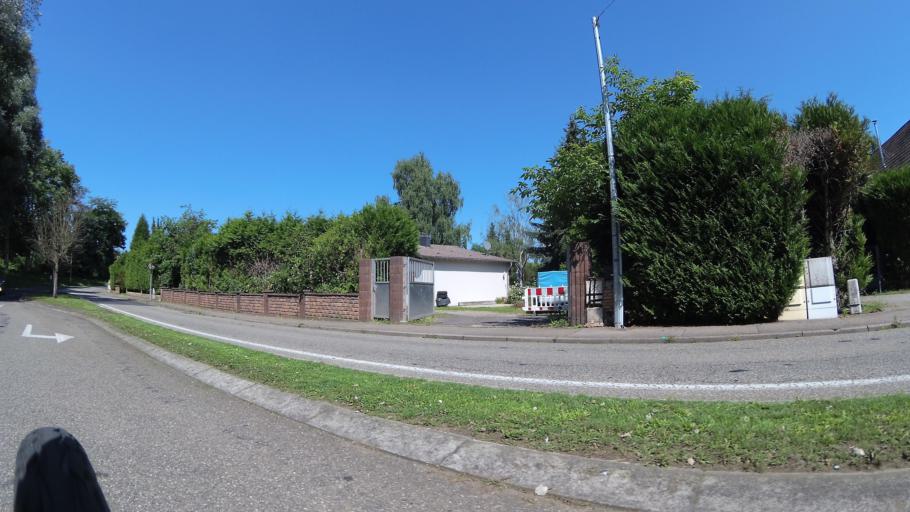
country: FR
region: Lorraine
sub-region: Departement de la Moselle
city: Stiring-Wendel
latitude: 49.2058
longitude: 6.9365
